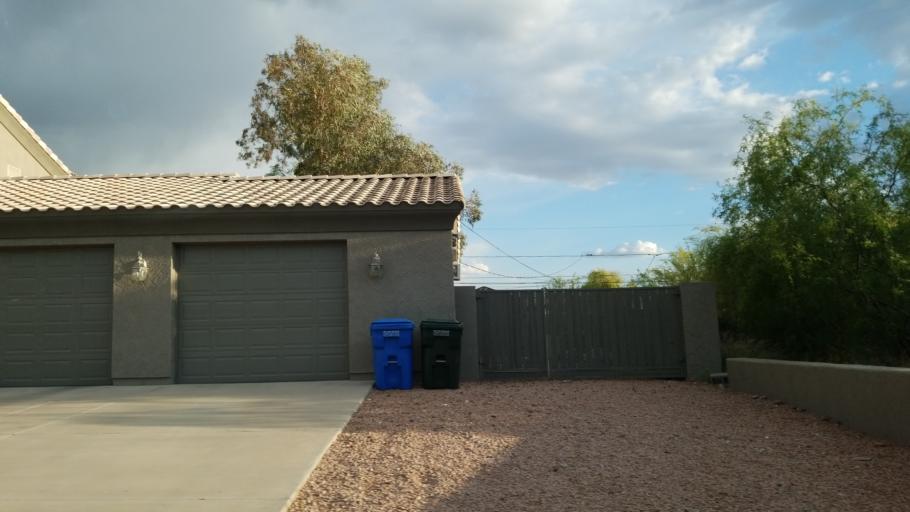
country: US
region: Arizona
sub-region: Maricopa County
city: Paradise Valley
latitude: 33.5887
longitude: -112.0538
